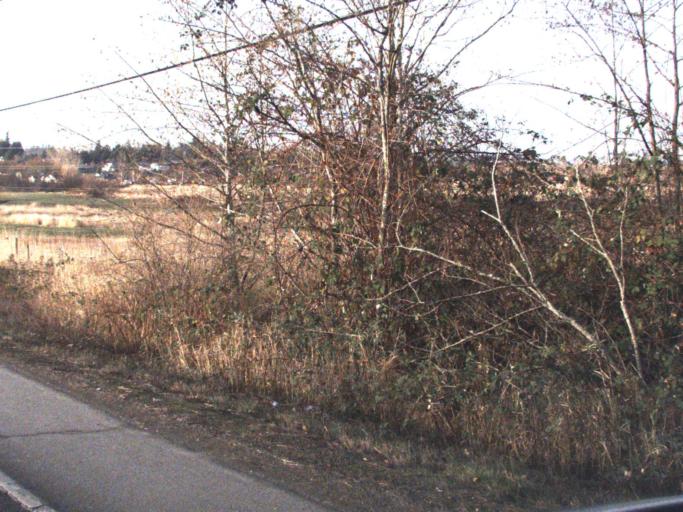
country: US
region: Washington
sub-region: Skagit County
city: Big Lake
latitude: 48.4349
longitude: -122.2802
